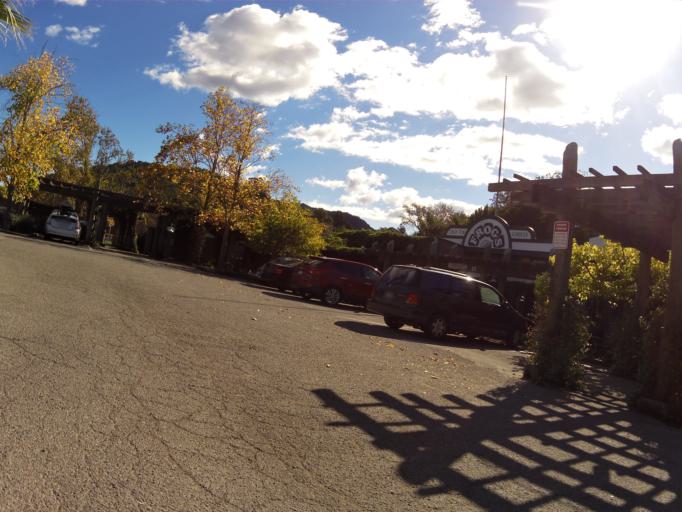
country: US
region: California
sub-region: Marin County
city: Fairfax
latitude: 37.9875
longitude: -122.5914
